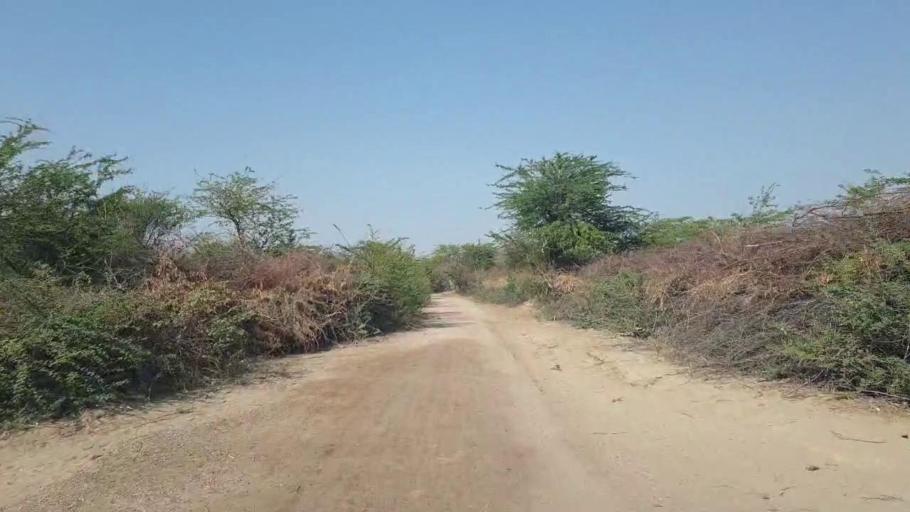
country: PK
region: Sindh
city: Dhoro Naro
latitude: 25.5026
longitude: 69.6042
